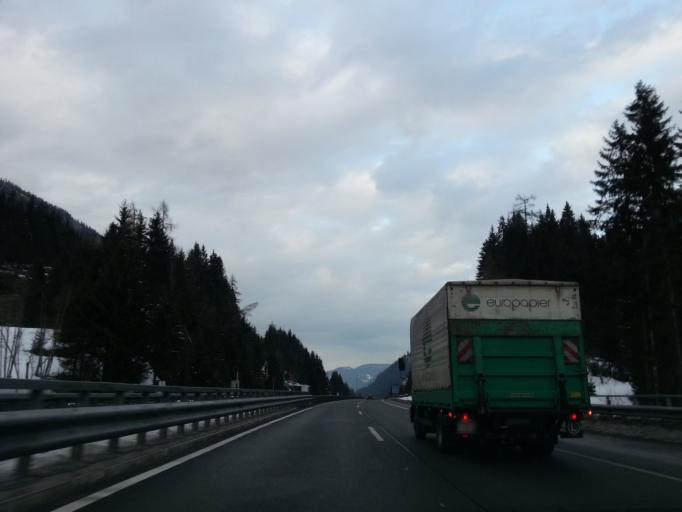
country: AT
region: Salzburg
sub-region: Politischer Bezirk Sankt Johann im Pongau
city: Flachau
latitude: 47.3012
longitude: 13.3923
